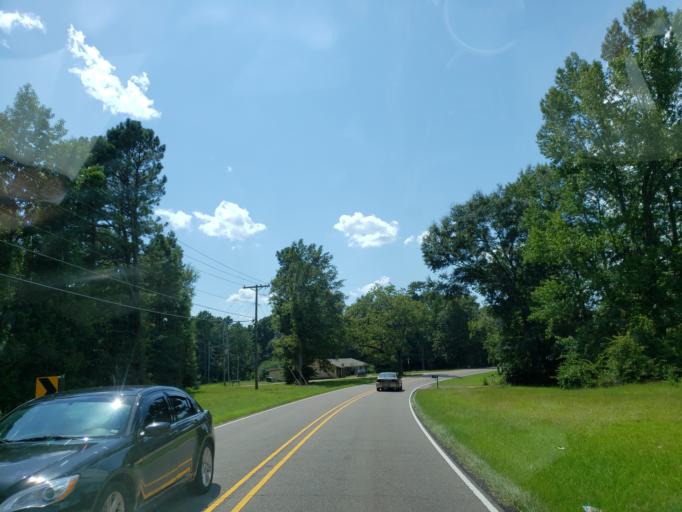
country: US
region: Mississippi
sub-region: Lamar County
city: West Hattiesburg
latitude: 31.2892
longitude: -89.3964
